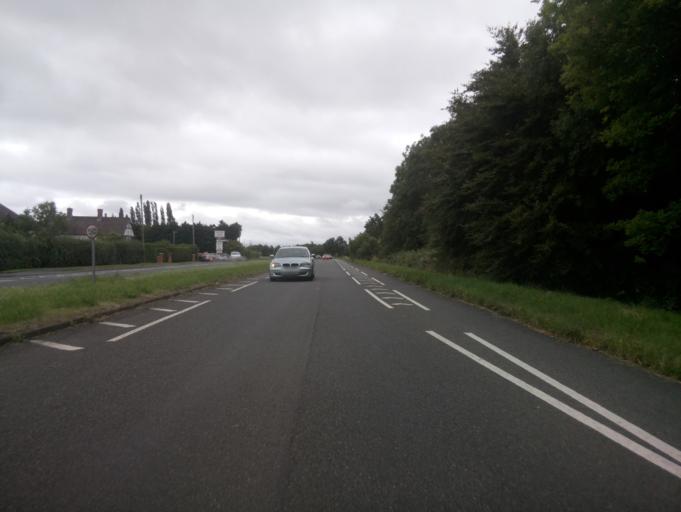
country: GB
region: England
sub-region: Gloucestershire
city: Tewkesbury
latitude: 51.9651
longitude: -2.1583
